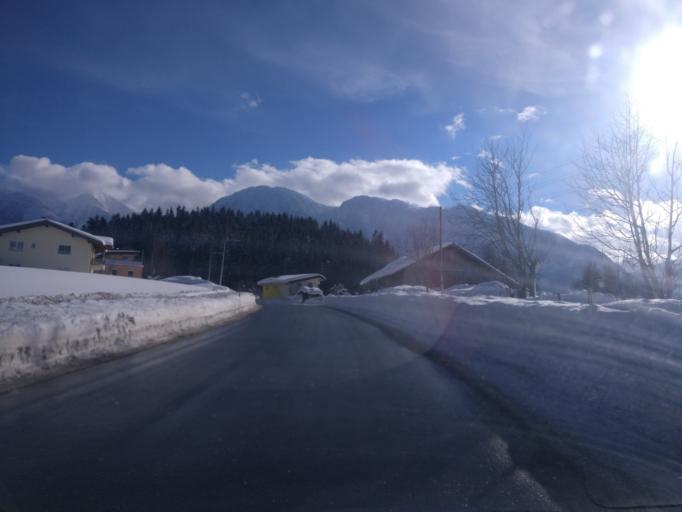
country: AT
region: Salzburg
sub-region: Politischer Bezirk Sankt Johann im Pongau
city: Goldegg
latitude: 47.3239
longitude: 13.0846
